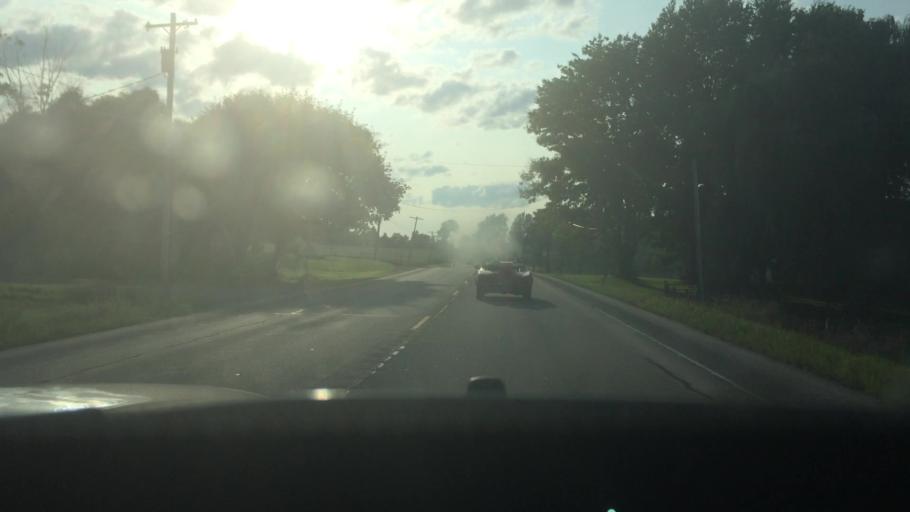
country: US
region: New York
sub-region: St. Lawrence County
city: Ogdensburg
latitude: 44.6642
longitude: -75.3484
